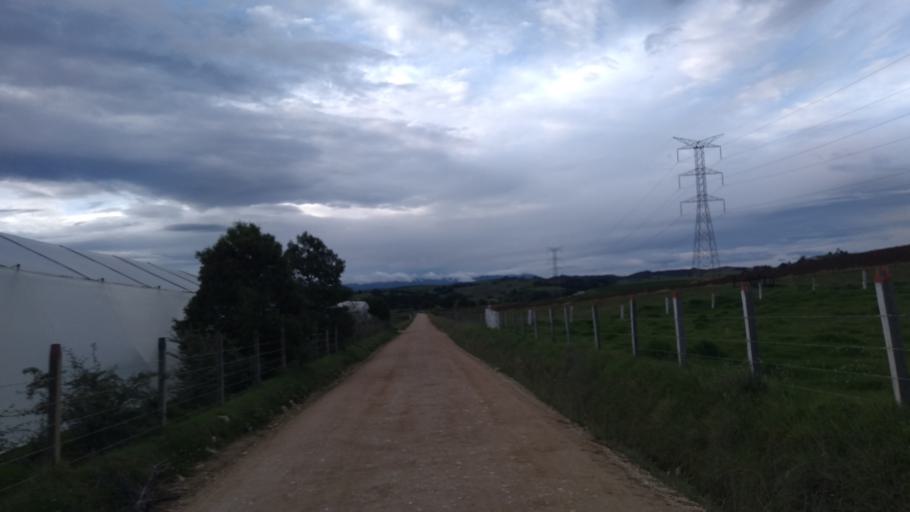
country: CO
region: Boyaca
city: Toca
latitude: 5.6071
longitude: -73.1764
